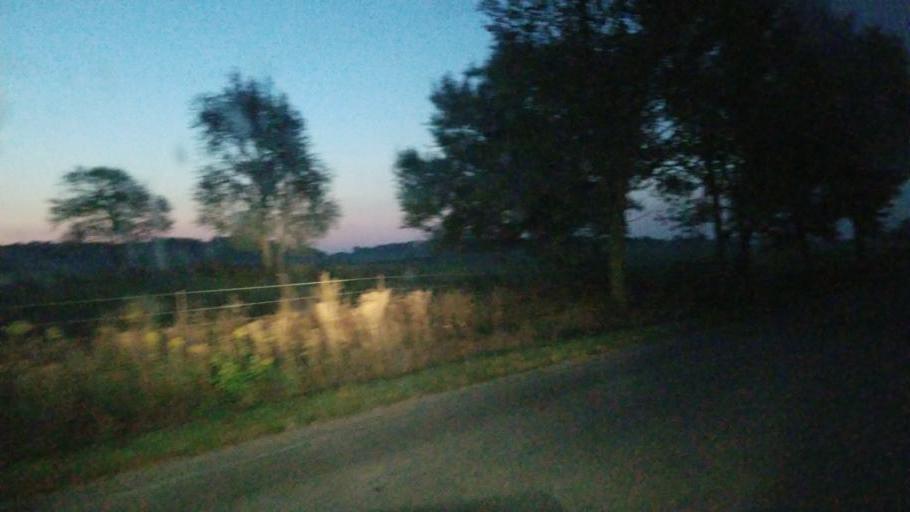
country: US
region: Indiana
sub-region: Elkhart County
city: Middlebury
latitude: 41.6906
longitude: -85.6680
